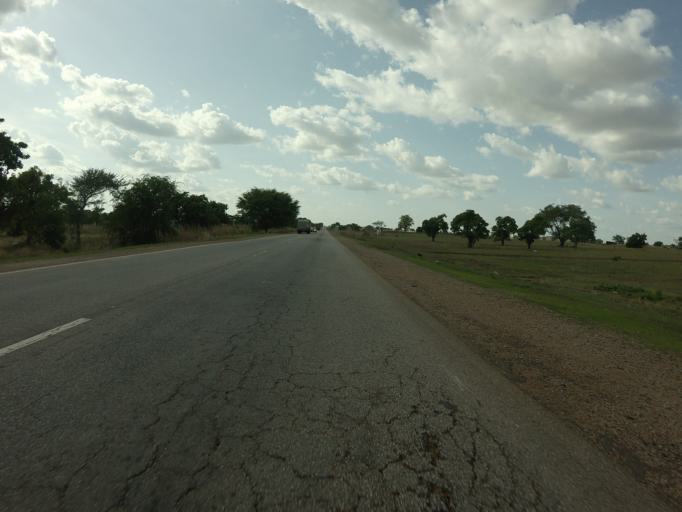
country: GH
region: Upper East
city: Bolgatanga
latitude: 10.6675
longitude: -0.8603
